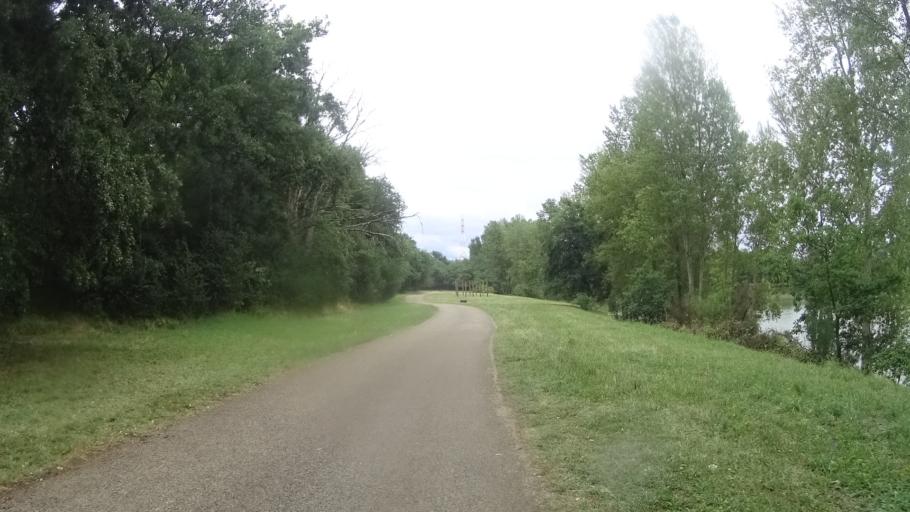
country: FR
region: Centre
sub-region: Departement du Loiret
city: Saint-Jean-de-Braye
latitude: 47.8995
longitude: 1.9696
